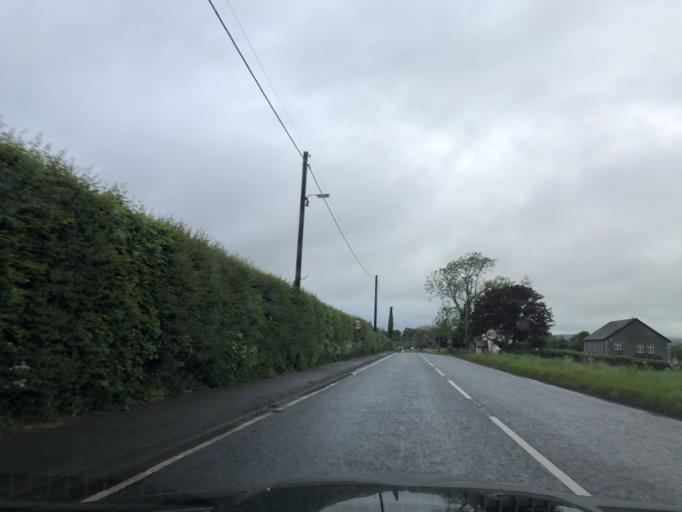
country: GB
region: Northern Ireland
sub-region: Antrim Borough
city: Antrim
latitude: 54.7030
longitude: -6.2229
